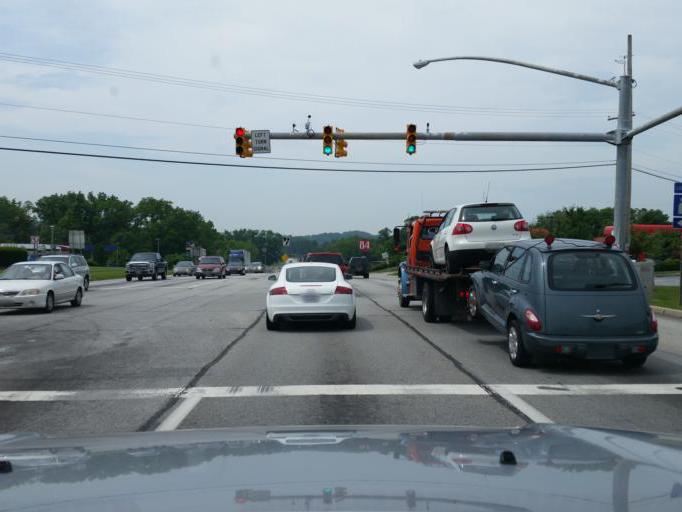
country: US
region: Pennsylvania
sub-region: York County
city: Dillsburg
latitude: 40.1173
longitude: -77.0374
